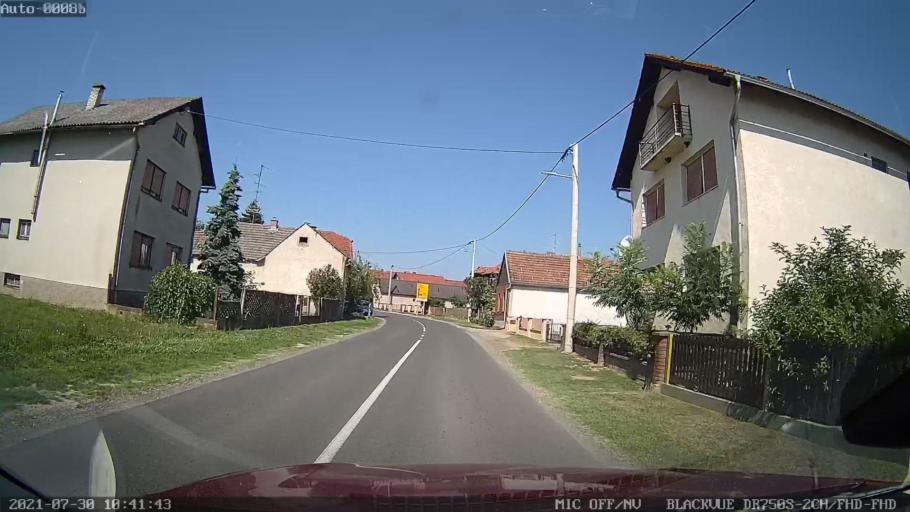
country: HR
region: Medimurska
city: Kursanec
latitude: 46.2817
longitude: 16.4122
